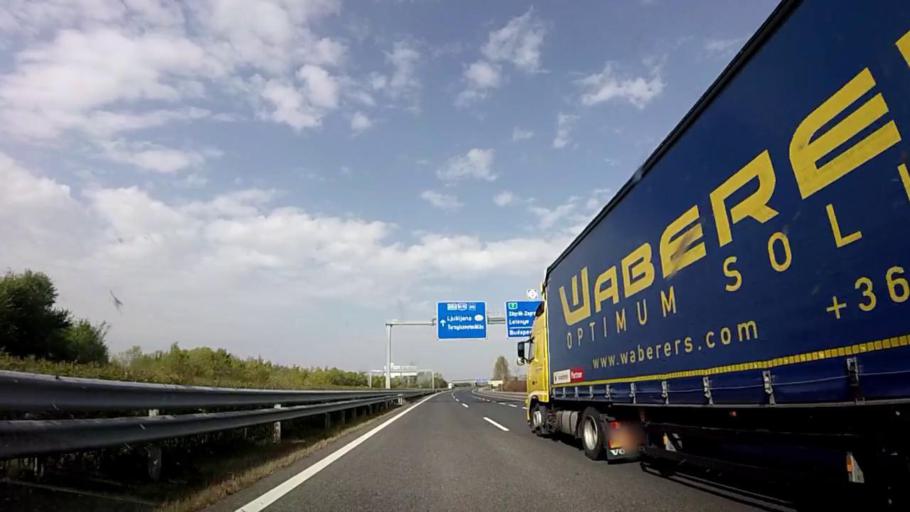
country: HU
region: Zala
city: Letenye
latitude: 46.4193
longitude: 16.7148
